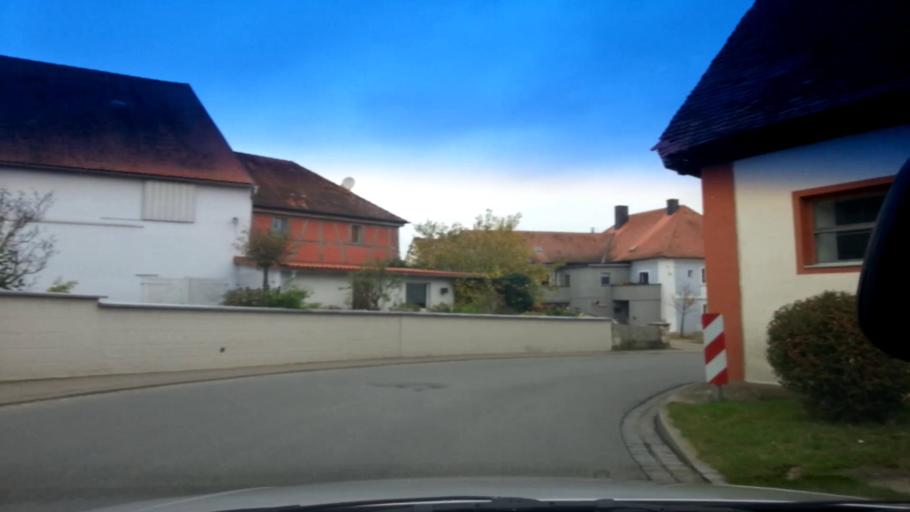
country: DE
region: Bavaria
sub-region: Upper Franconia
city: Burgebrach
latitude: 49.8257
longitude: 10.7781
